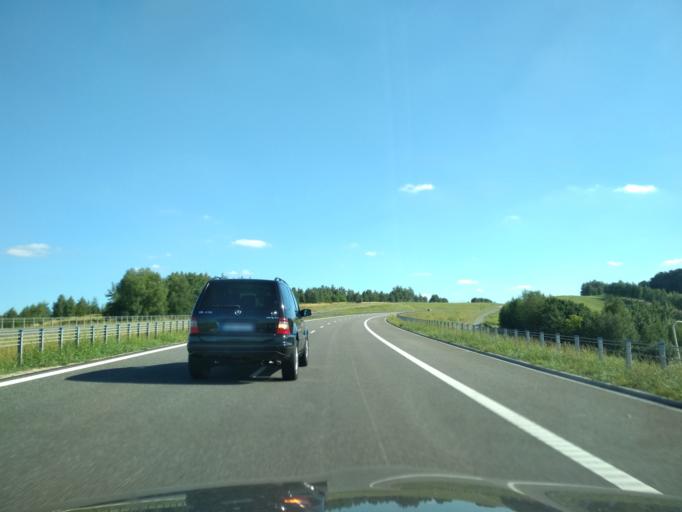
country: PL
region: Subcarpathian Voivodeship
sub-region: Rzeszow
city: Przybyszowka
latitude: 50.0427
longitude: 21.9336
